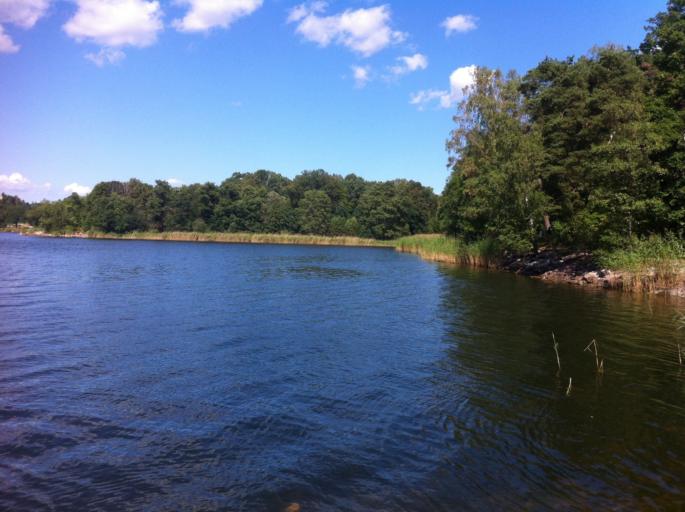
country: SE
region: Stockholm
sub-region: Norrtalje Kommun
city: Bergshamra
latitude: 59.3881
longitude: 18.0311
